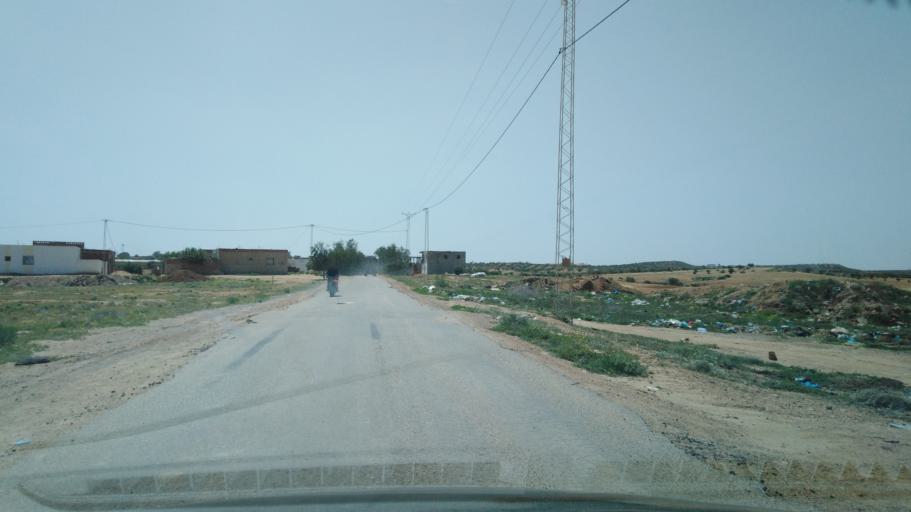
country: TN
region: Safaqis
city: Sfax
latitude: 34.7258
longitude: 10.5294
